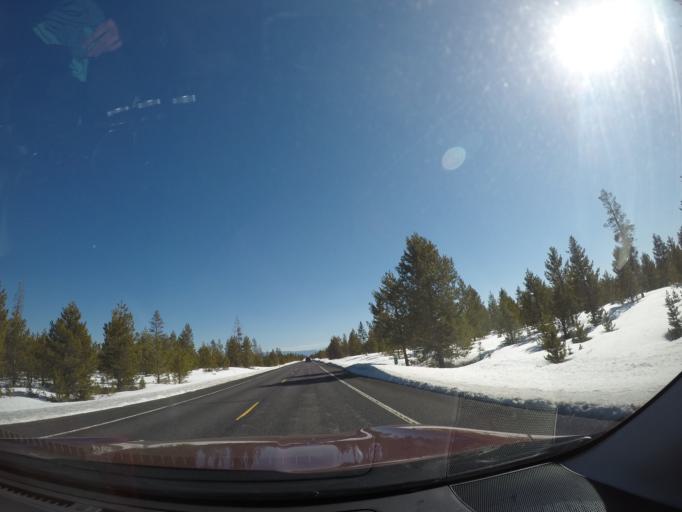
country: US
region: Oregon
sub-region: Deschutes County
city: Three Rivers
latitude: 43.8852
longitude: -121.5761
